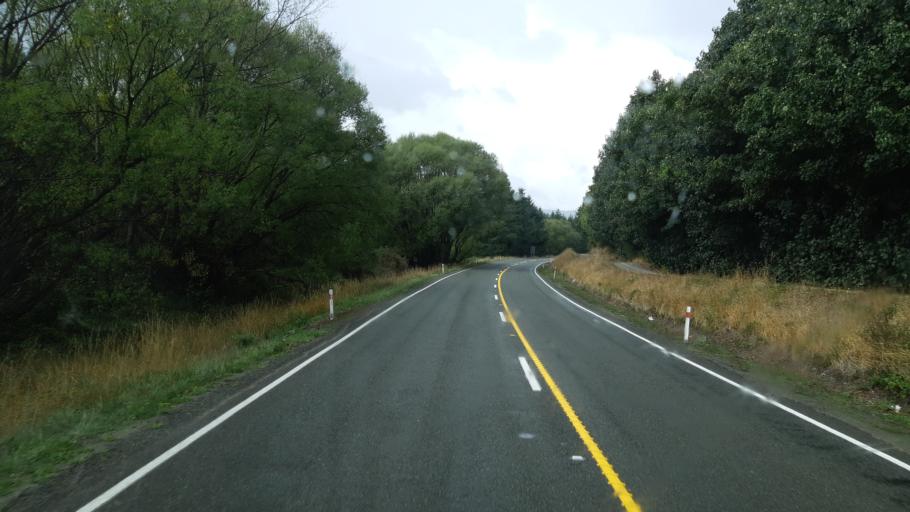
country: NZ
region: Tasman
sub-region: Tasman District
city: Wakefield
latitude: -41.4757
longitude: 172.8566
